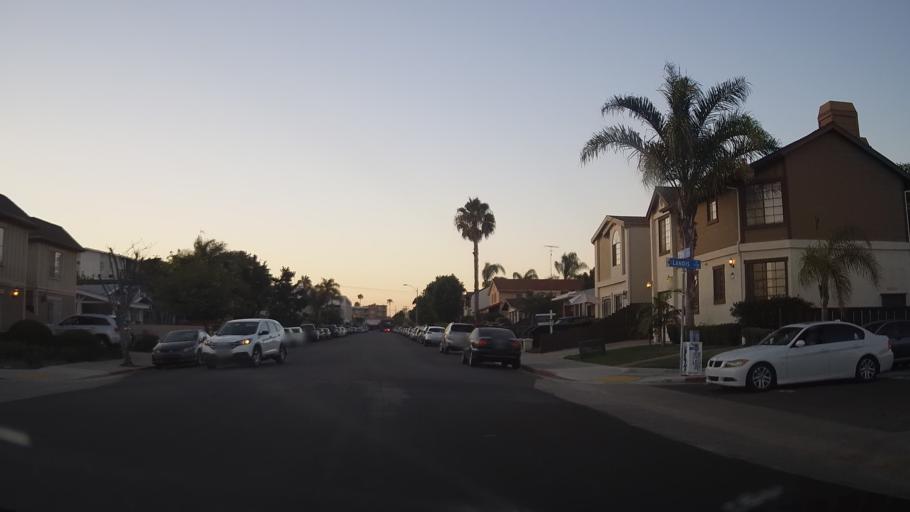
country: US
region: California
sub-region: San Diego County
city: San Diego
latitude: 32.7455
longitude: -117.1272
